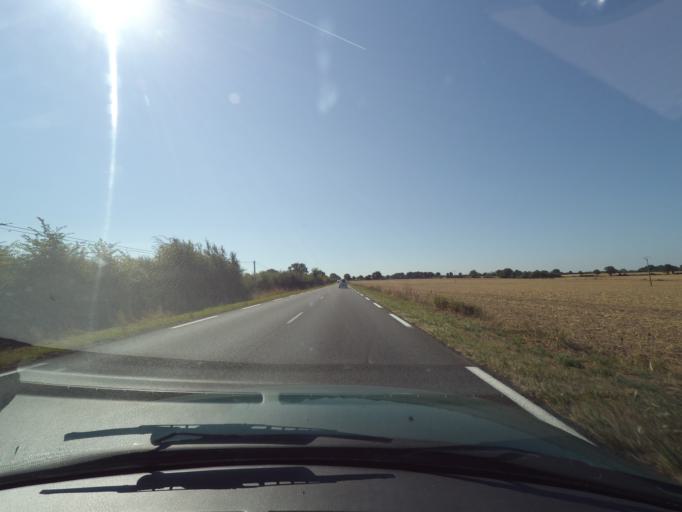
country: FR
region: Poitou-Charentes
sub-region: Departement de la Vienne
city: Saulge
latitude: 46.3088
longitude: 0.8311
